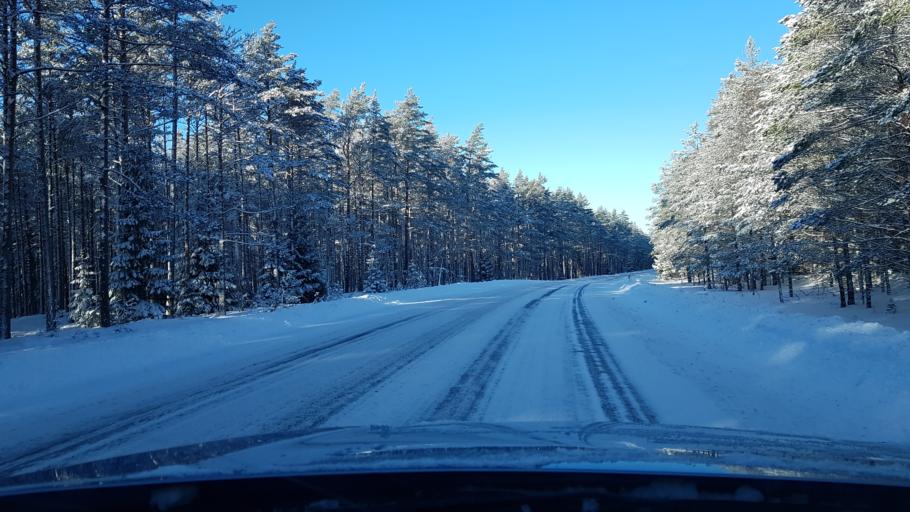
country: EE
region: Hiiumaa
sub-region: Kaerdla linn
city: Kardla
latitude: 58.9281
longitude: 22.7852
